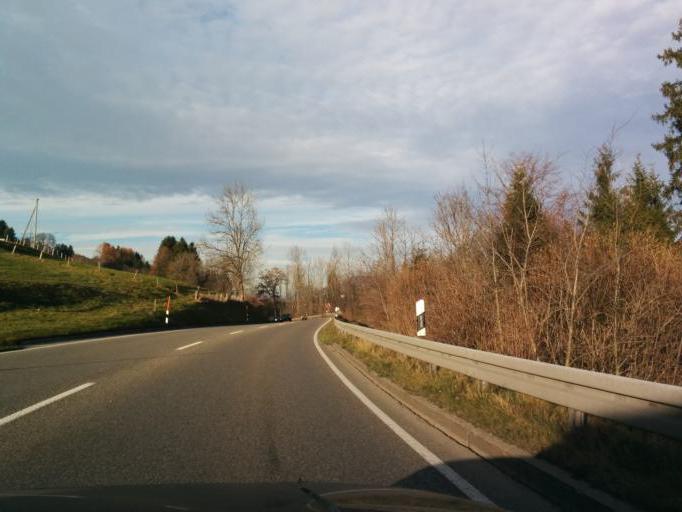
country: DE
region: Bavaria
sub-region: Swabia
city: Sonthofen
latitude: 47.4873
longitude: 10.2669
